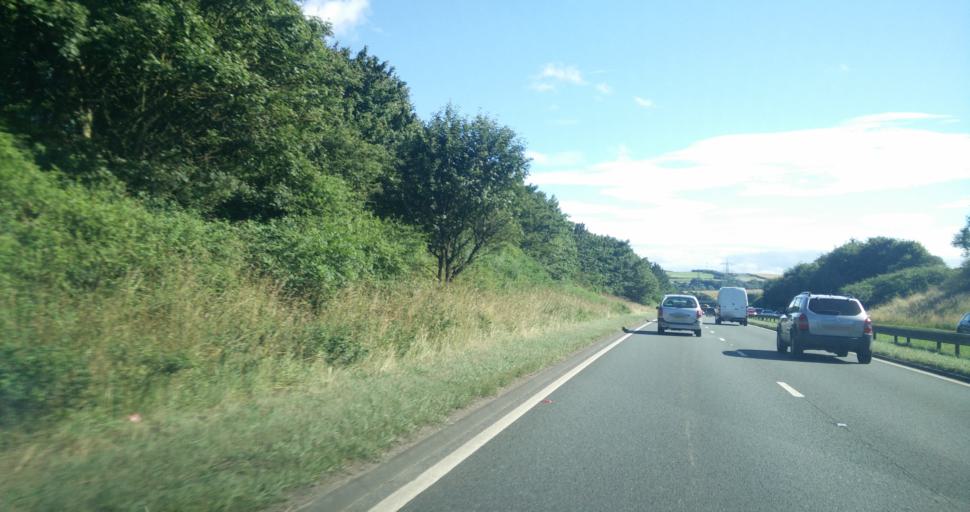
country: GB
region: England
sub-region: County Durham
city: Houghton-le-Spring
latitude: 54.8770
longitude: -1.4521
